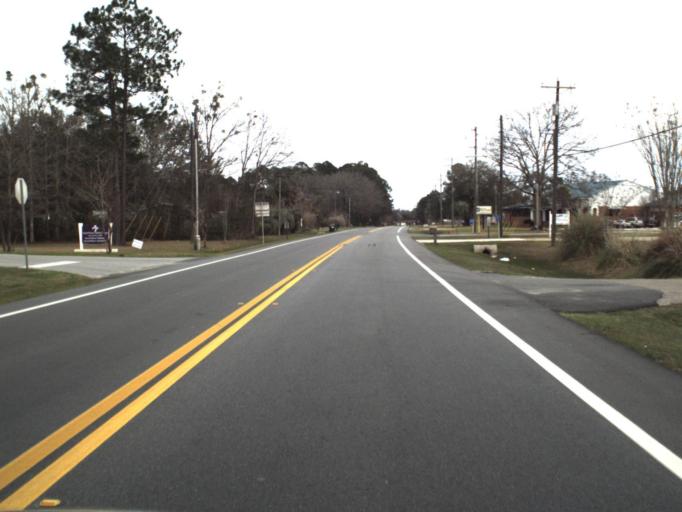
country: US
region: Florida
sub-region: Gulf County
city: Wewahitchka
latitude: 30.1187
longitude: -85.2105
